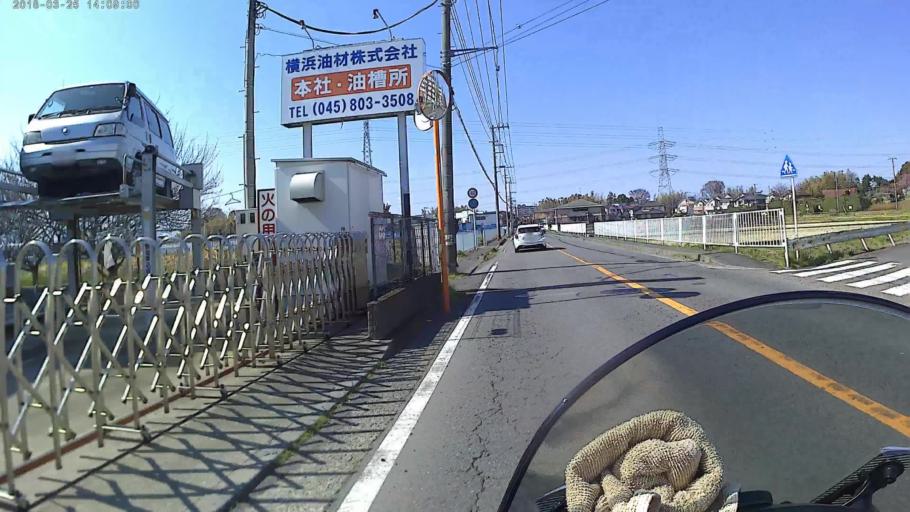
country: JP
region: Kanagawa
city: Minami-rinkan
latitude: 35.4216
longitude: 139.4777
